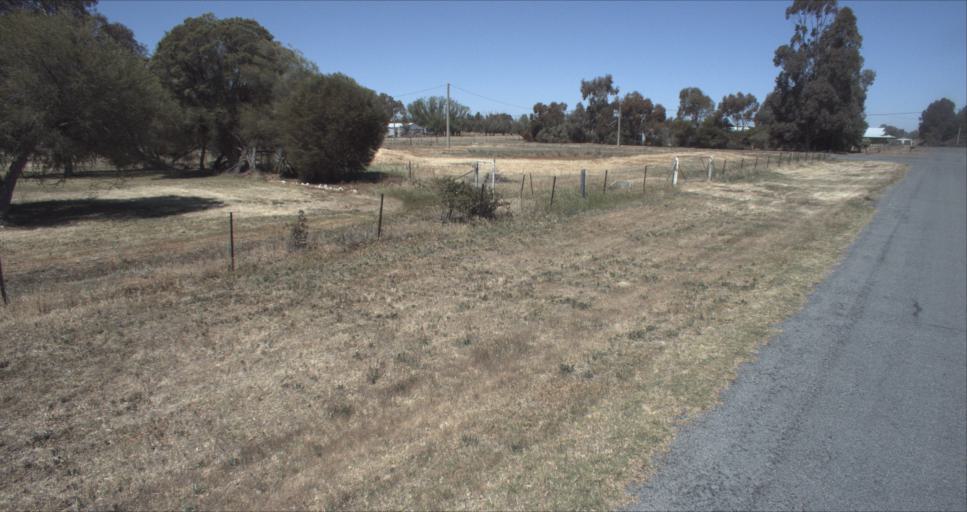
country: AU
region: New South Wales
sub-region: Leeton
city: Leeton
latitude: -34.5198
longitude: 146.4040
